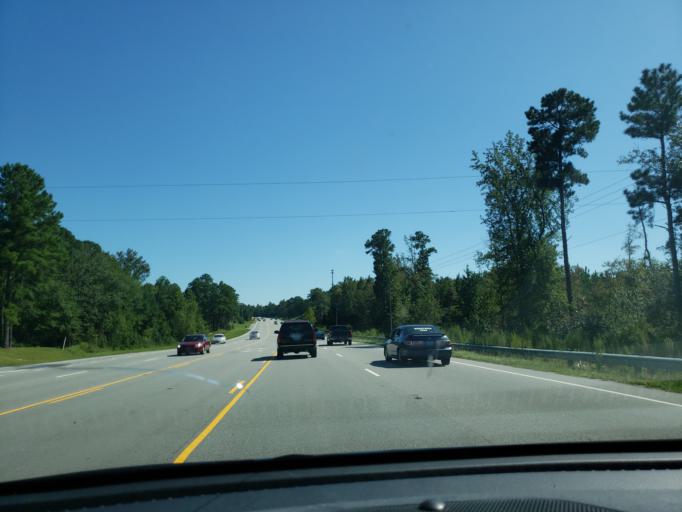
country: US
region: North Carolina
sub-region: Lee County
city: Broadway
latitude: 35.3506
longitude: -79.1085
